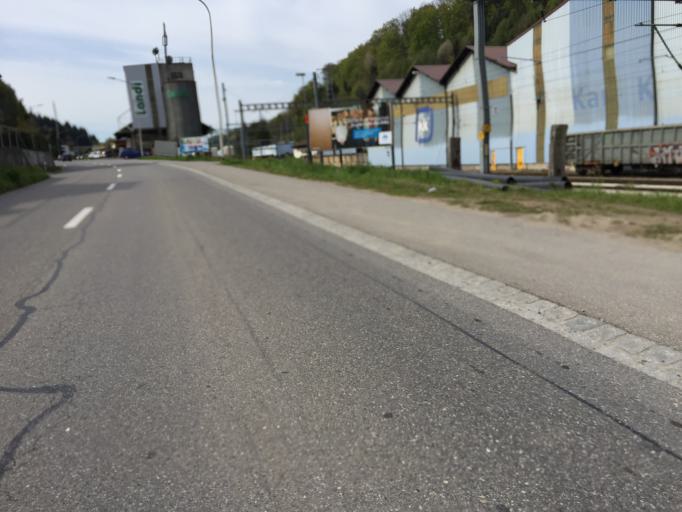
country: CH
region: Fribourg
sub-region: Sense District
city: Flamatt
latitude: 46.9038
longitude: 7.3567
